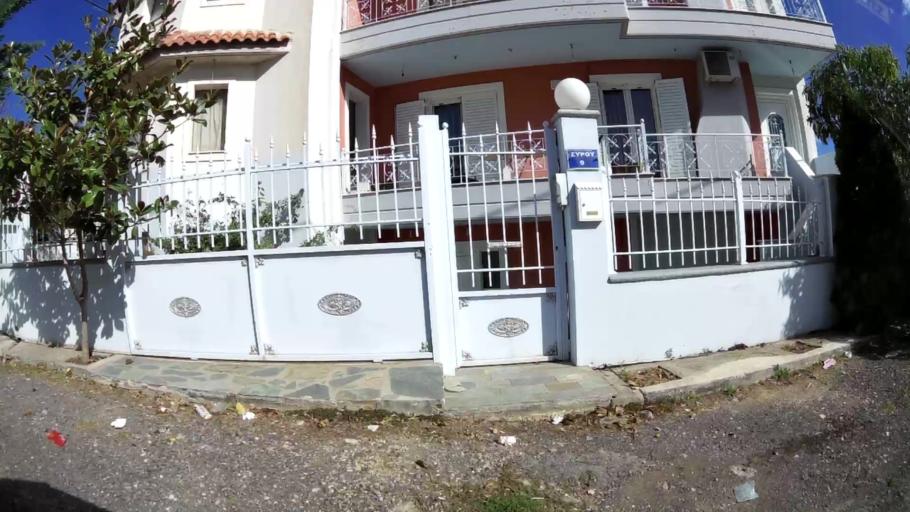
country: GR
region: Attica
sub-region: Nomarchia Anatolikis Attikis
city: Thrakomakedones
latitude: 38.1159
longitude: 23.7303
